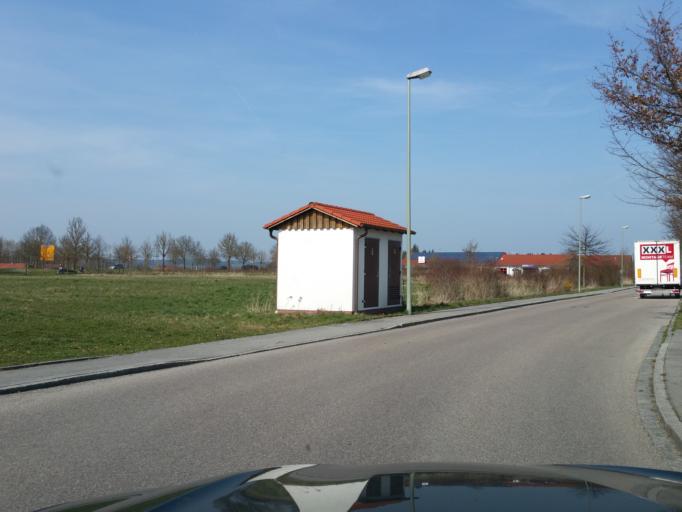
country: DE
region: Bavaria
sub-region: Upper Bavaria
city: Moosburg
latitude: 48.4680
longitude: 11.9608
